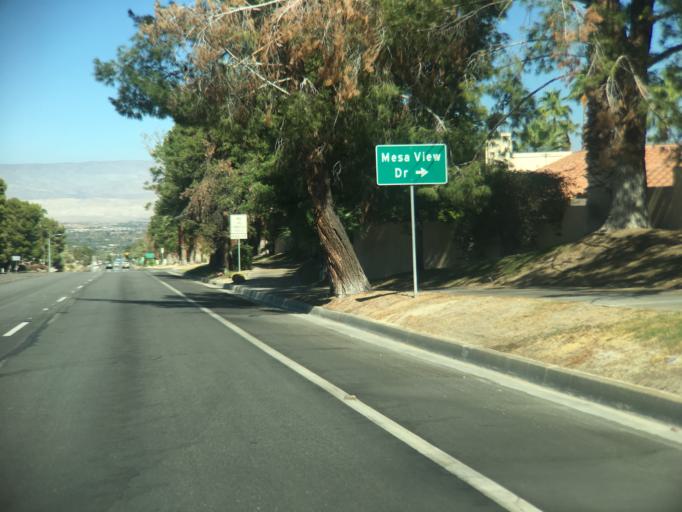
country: US
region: California
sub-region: Riverside County
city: Palm Desert
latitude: 33.6947
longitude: -116.4005
